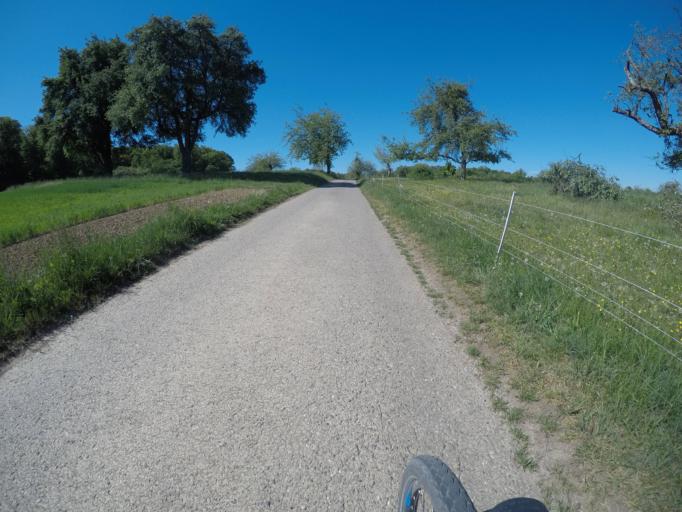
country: DE
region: Baden-Wuerttemberg
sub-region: Regierungsbezirk Stuttgart
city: Weissach
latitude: 48.8368
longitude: 8.8985
